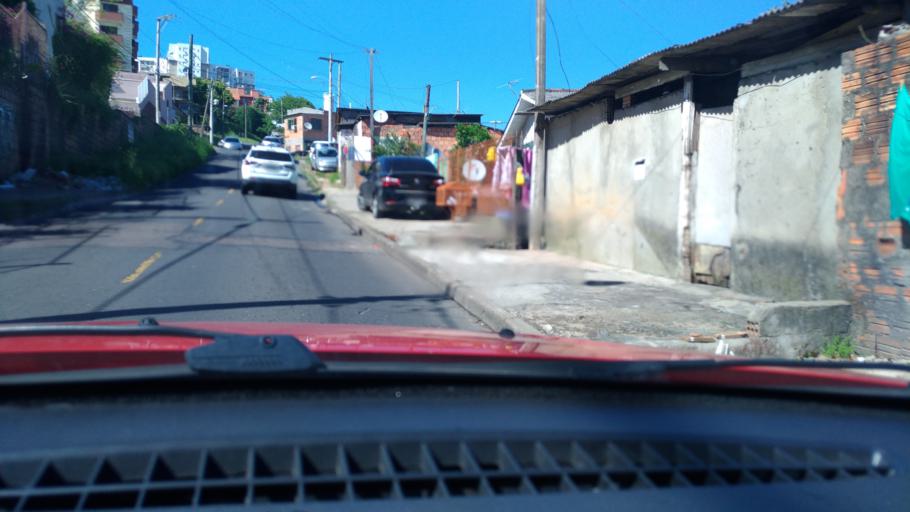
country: BR
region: Rio Grande do Sul
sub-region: Porto Alegre
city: Porto Alegre
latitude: -30.0322
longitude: -51.1478
